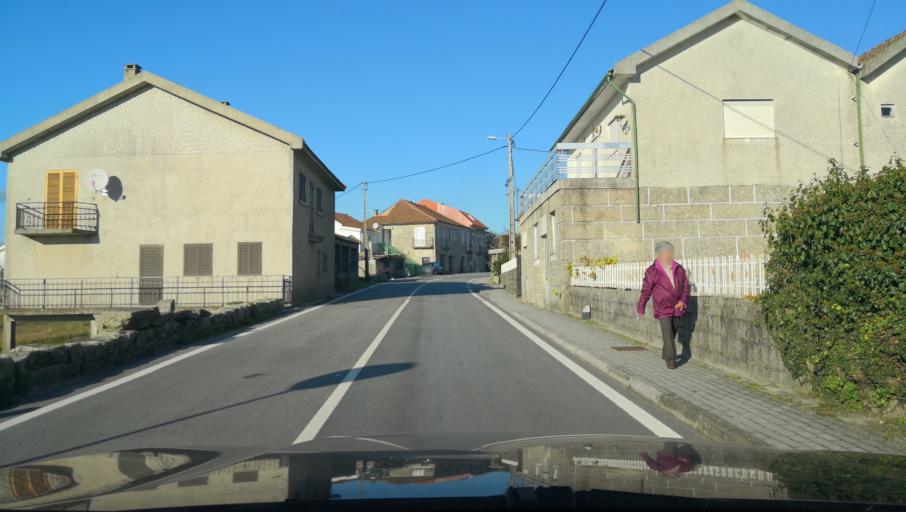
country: PT
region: Vila Real
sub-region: Vila Real
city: Vila Real
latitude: 41.3350
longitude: -7.6643
